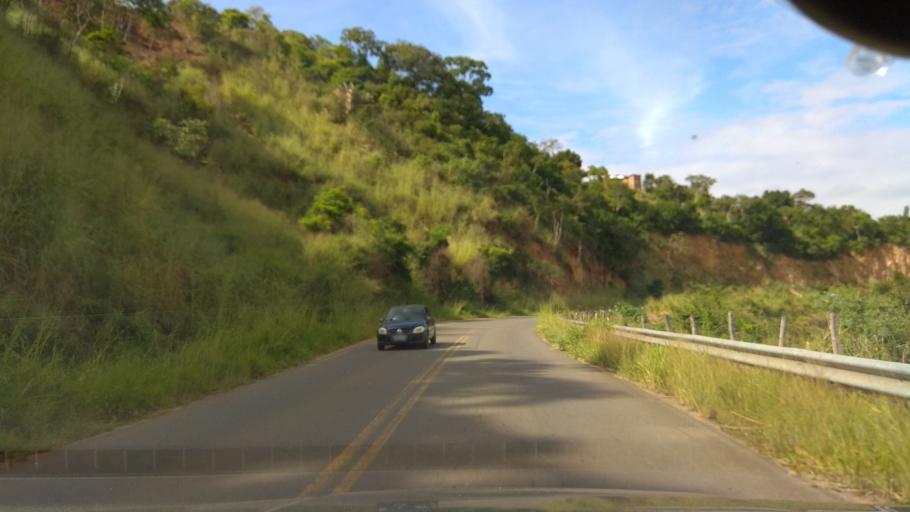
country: BR
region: Bahia
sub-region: Ubaira
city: Ubaira
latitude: -13.2563
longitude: -39.6635
